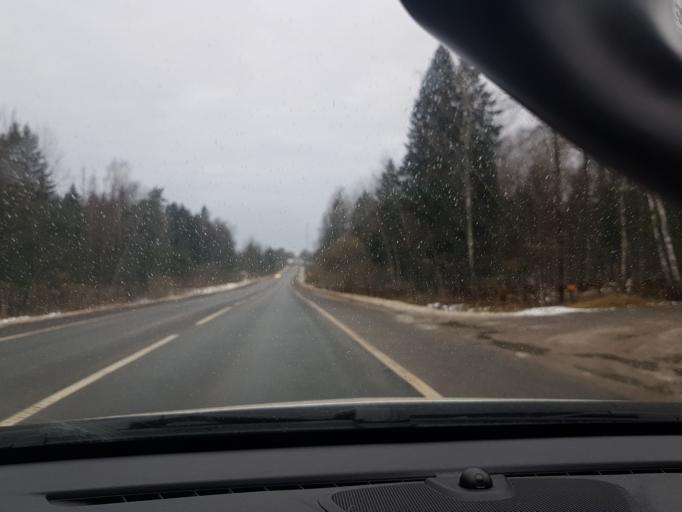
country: RU
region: Moskovskaya
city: Sychevo
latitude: 56.0088
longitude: 36.2092
